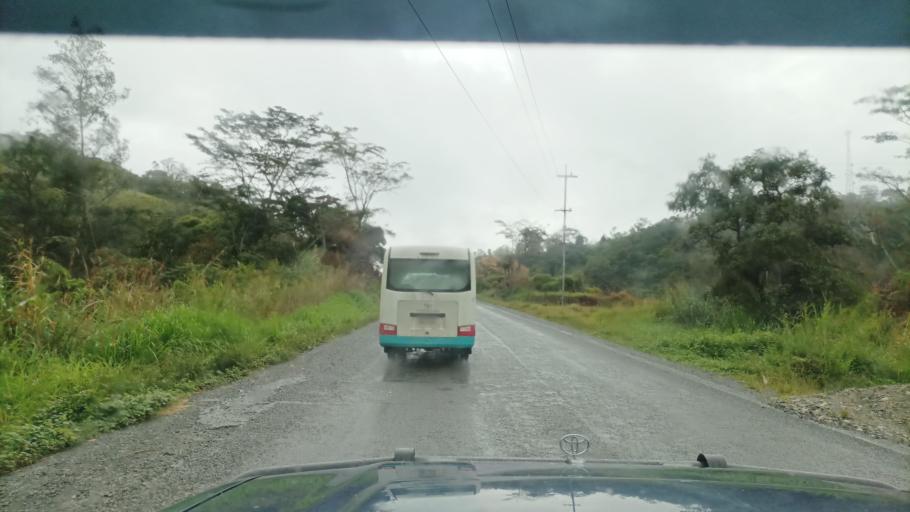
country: PG
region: Western Highlands
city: Rauna
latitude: -5.8294
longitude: 144.3699
